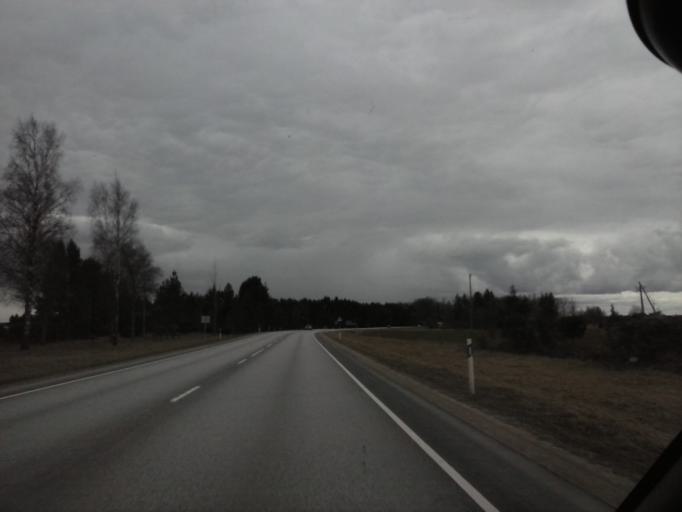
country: EE
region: Jaervamaa
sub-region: Paide linn
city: Paide
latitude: 58.8441
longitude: 25.7379
